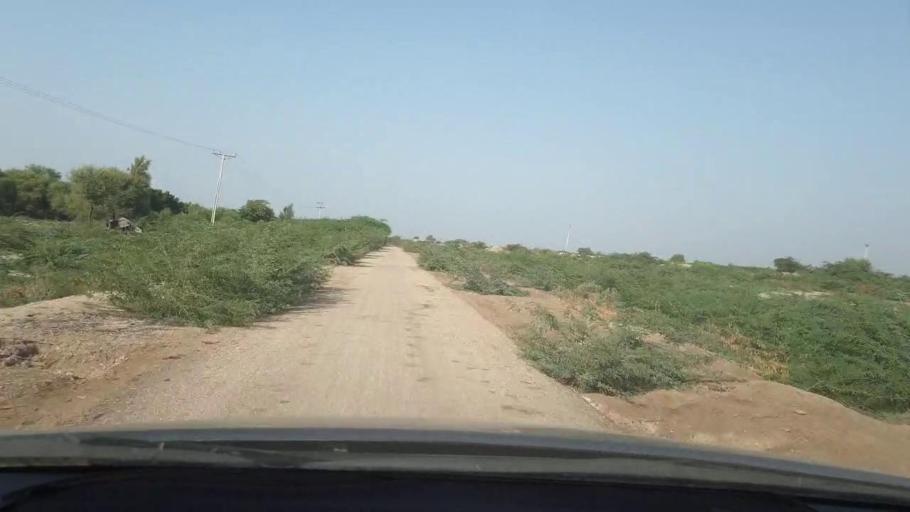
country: PK
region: Sindh
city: Naukot
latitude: 24.7875
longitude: 69.2964
